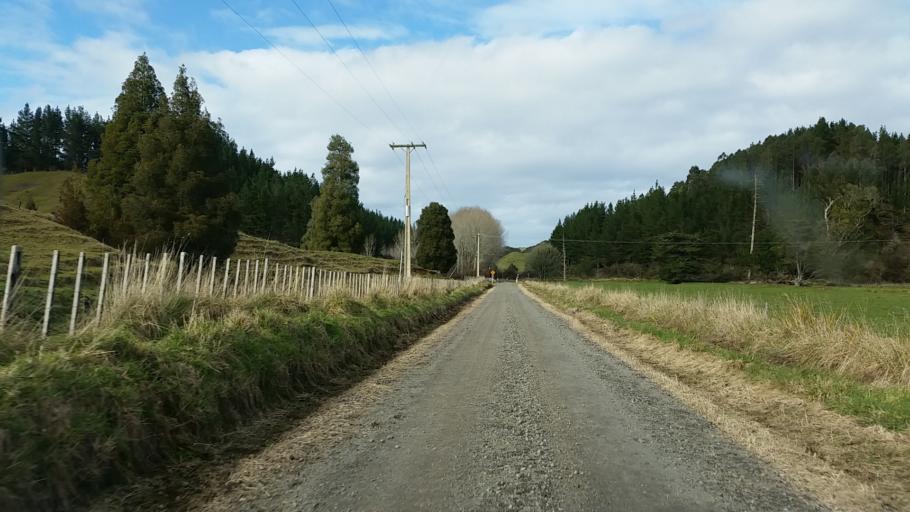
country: NZ
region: Taranaki
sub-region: South Taranaki District
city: Eltham
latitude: -39.2315
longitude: 174.5667
